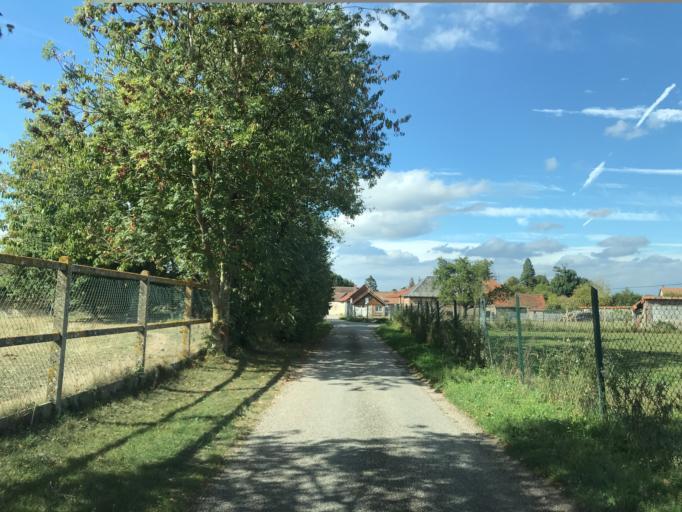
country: FR
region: Haute-Normandie
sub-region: Departement de l'Eure
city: Ande
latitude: 49.1912
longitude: 1.2434
